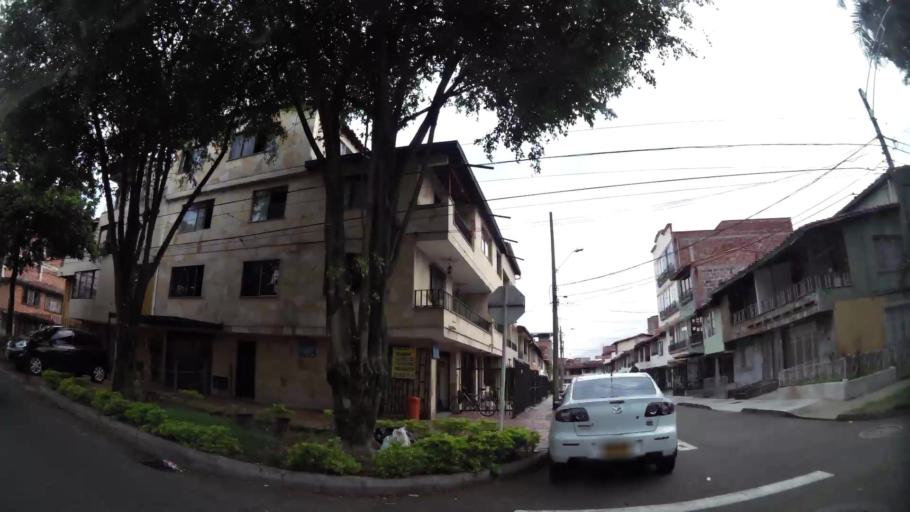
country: CO
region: Antioquia
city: Medellin
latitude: 6.2060
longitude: -75.5514
